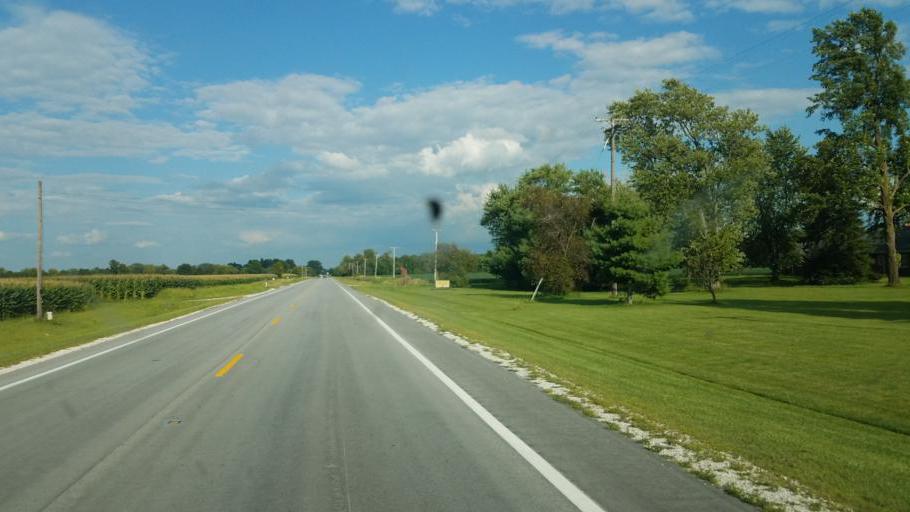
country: US
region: Ohio
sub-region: Sandusky County
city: Stony Prairie
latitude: 41.3418
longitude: -83.2009
